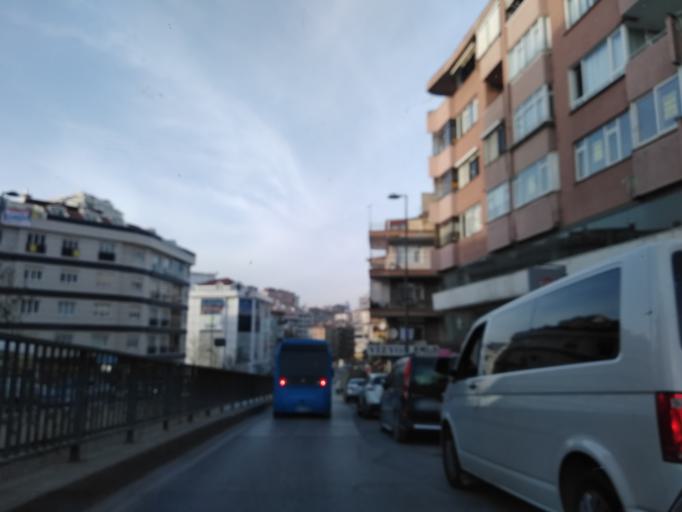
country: TR
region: Istanbul
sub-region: Atasehir
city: Atasehir
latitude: 40.9532
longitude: 29.1009
